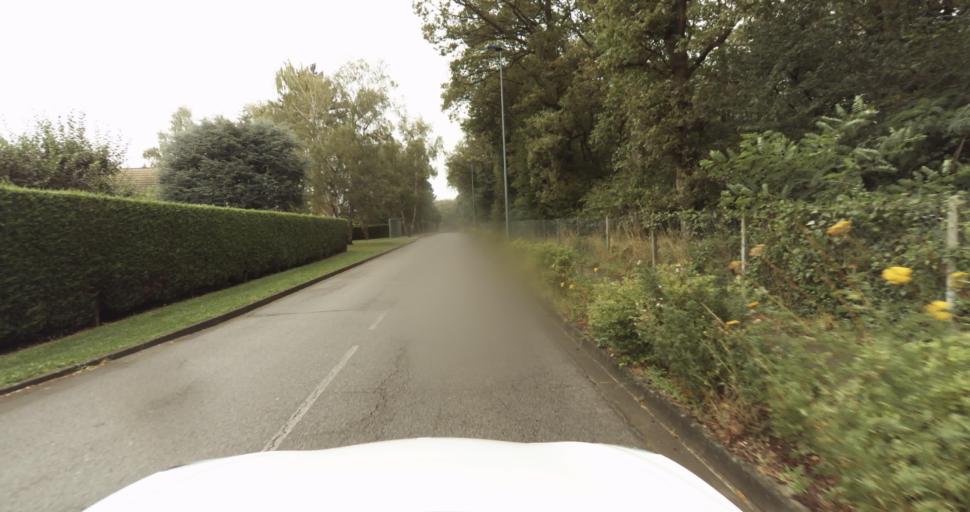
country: FR
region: Haute-Normandie
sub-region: Departement de l'Eure
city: Evreux
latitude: 49.0374
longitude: 1.1365
